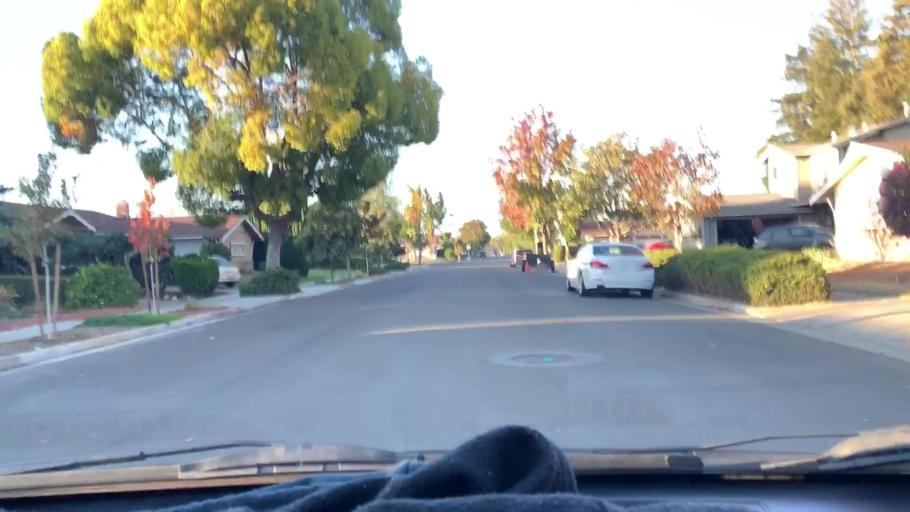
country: US
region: California
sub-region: Santa Clara County
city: Cupertino
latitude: 37.3255
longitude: -122.0178
